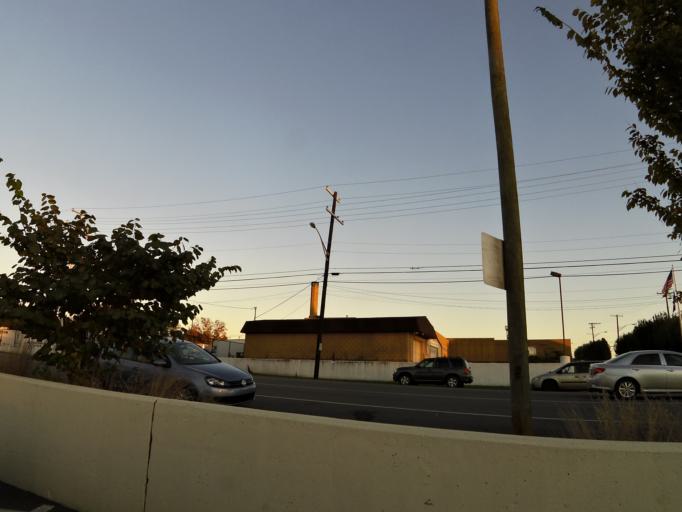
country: US
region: Tennessee
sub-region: Knox County
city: Knoxville
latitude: 35.9810
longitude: -83.9283
